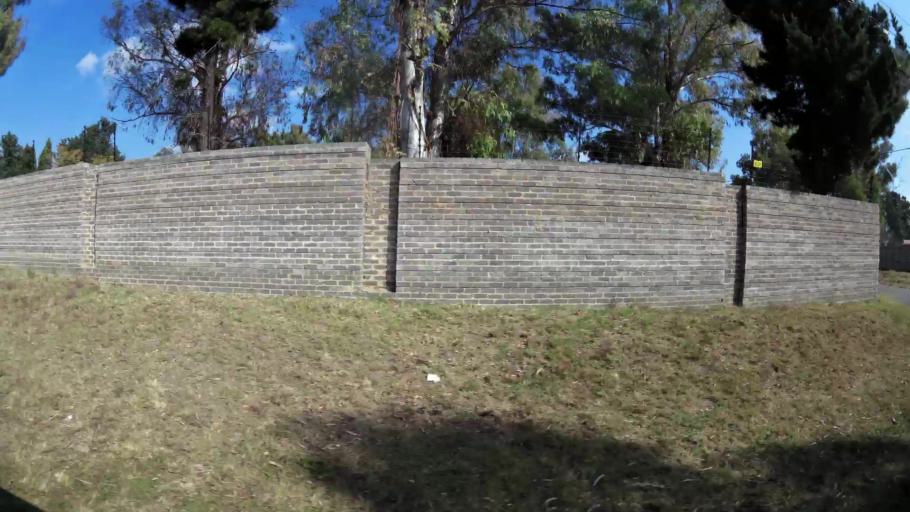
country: ZA
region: Gauteng
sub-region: Ekurhuleni Metropolitan Municipality
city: Benoni
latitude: -26.0843
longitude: 28.3556
